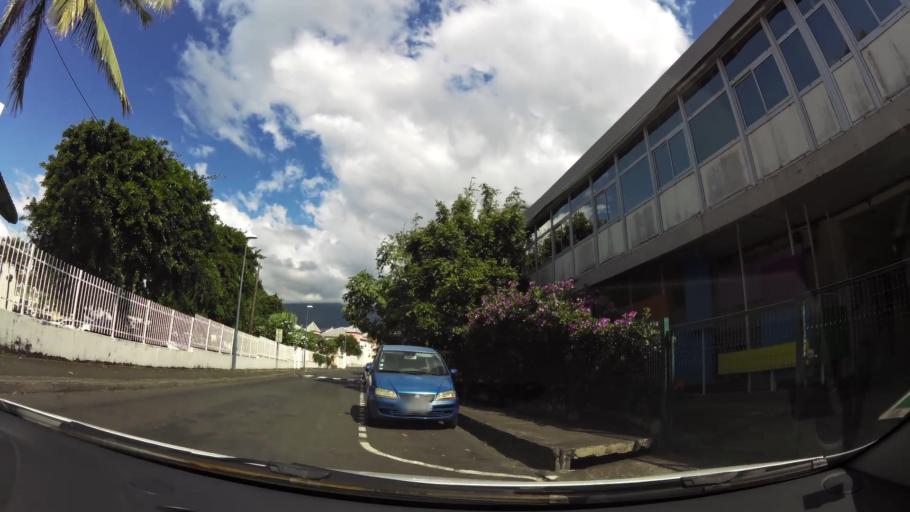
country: RE
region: Reunion
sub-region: Reunion
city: Saint-Denis
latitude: -20.8939
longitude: 55.4890
